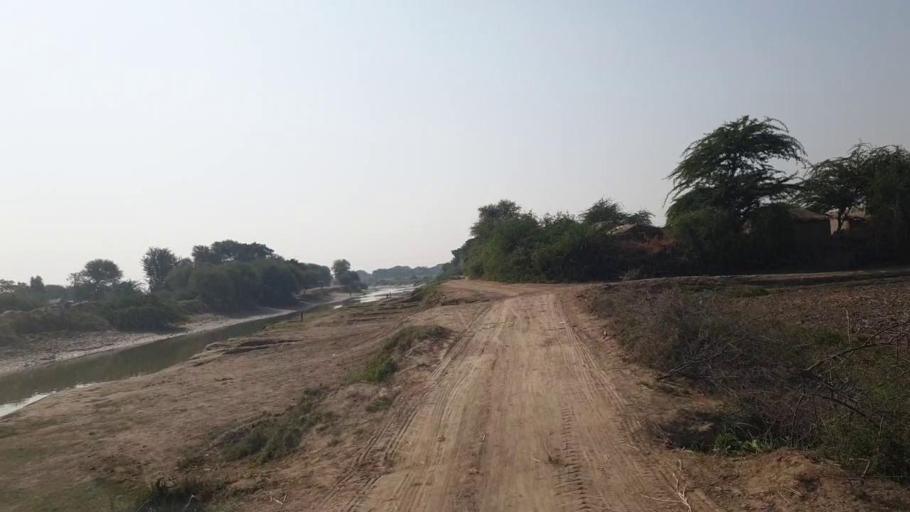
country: PK
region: Sindh
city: Matli
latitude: 24.9498
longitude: 68.6023
